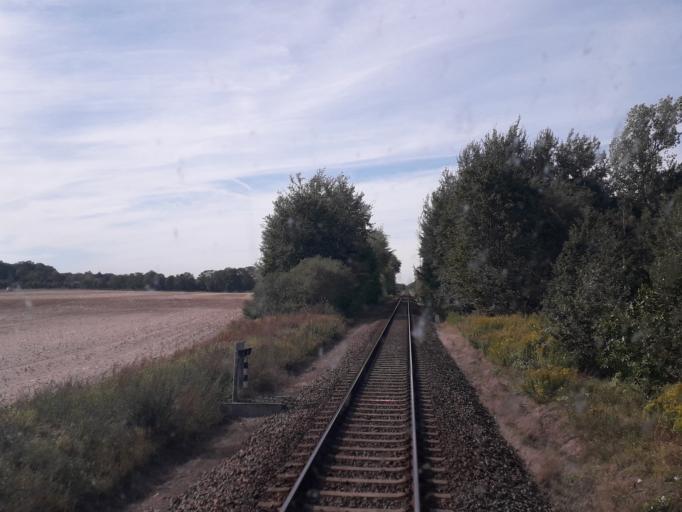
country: DE
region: Brandenburg
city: Kremmen
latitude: 52.7393
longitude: 13.0784
